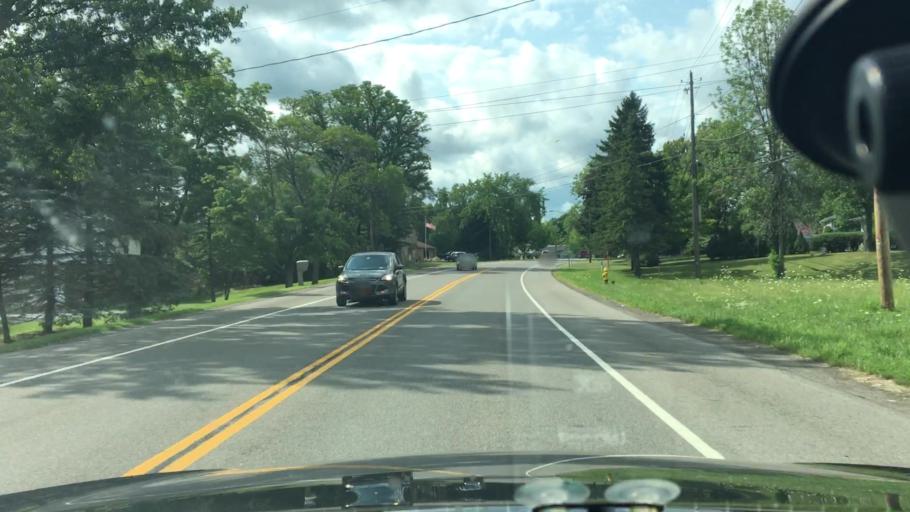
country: US
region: New York
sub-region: Erie County
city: North Boston
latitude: 42.6880
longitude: -78.7797
